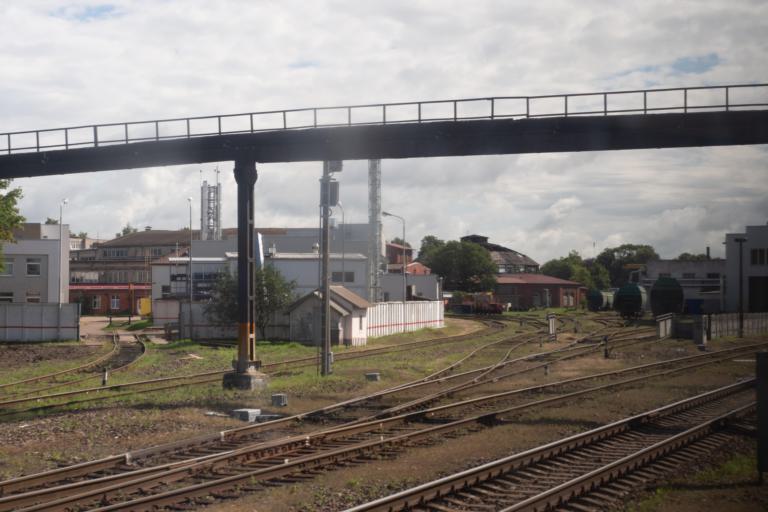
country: RU
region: Kaliningrad
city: Chernyakhovsk
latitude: 54.6297
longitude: 21.8106
